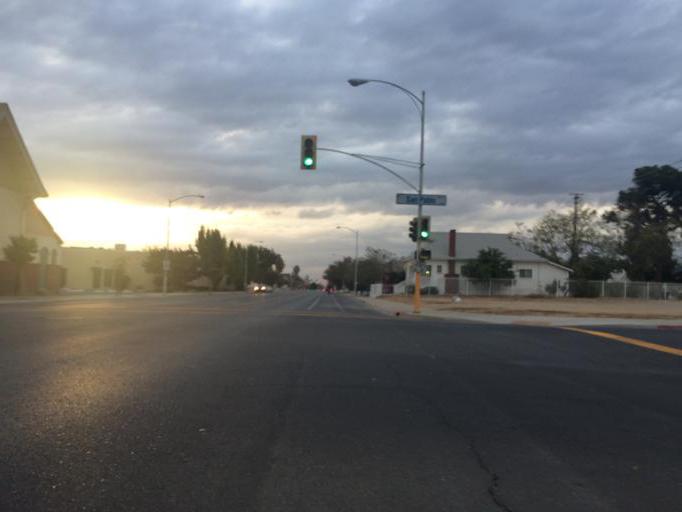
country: US
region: California
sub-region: Fresno County
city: Fresno
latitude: 36.7437
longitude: -119.7945
